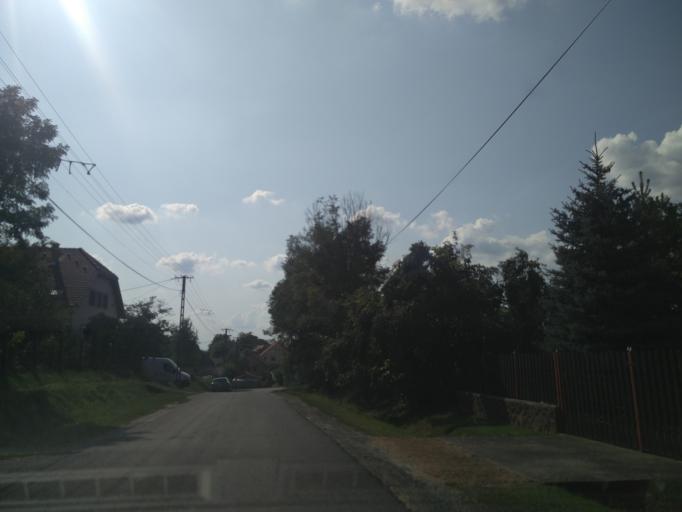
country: HU
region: Zala
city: Zalaegerszeg
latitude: 46.8974
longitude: 16.7705
